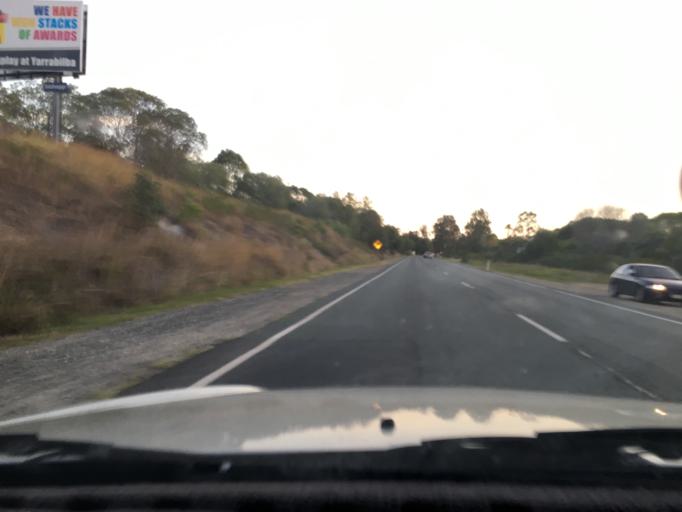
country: AU
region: Queensland
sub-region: Logan
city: Waterford West
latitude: -27.7044
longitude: 153.1475
